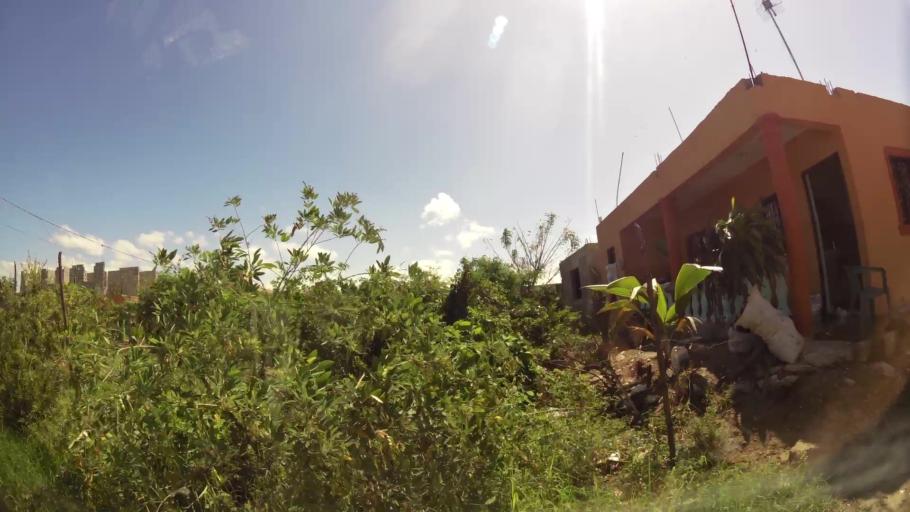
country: DO
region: San Cristobal
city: San Cristobal
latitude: 18.4264
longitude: -70.1306
